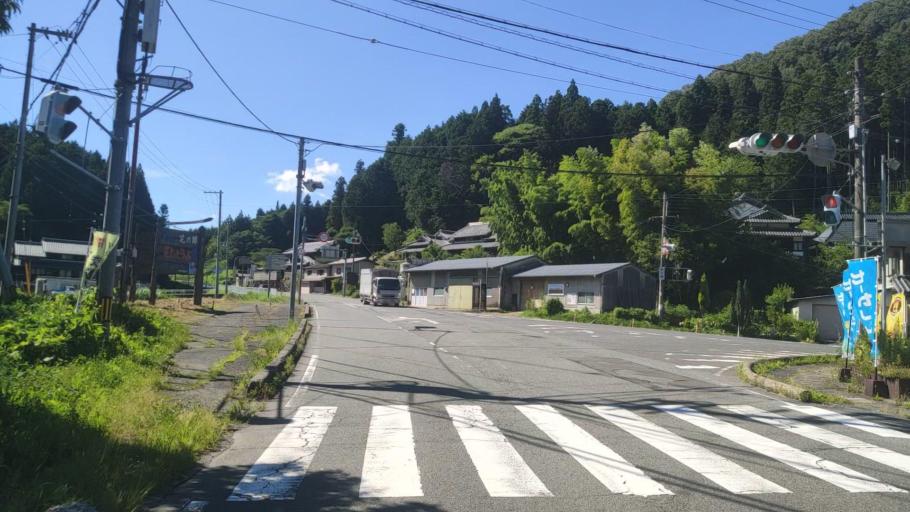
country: JP
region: Nara
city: Haibara-akanedai
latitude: 34.5847
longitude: 135.9687
